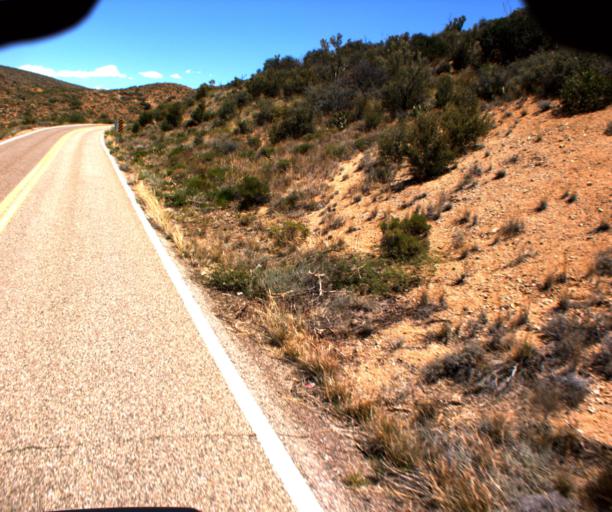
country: US
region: Arizona
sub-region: Yavapai County
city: Bagdad
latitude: 34.4465
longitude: -112.9681
